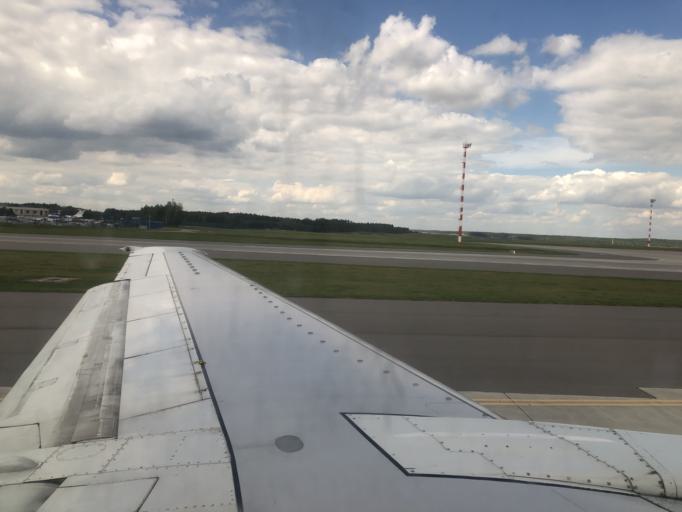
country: BY
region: Minsk
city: Horad Smalyavichy
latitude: 53.8897
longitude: 28.0441
